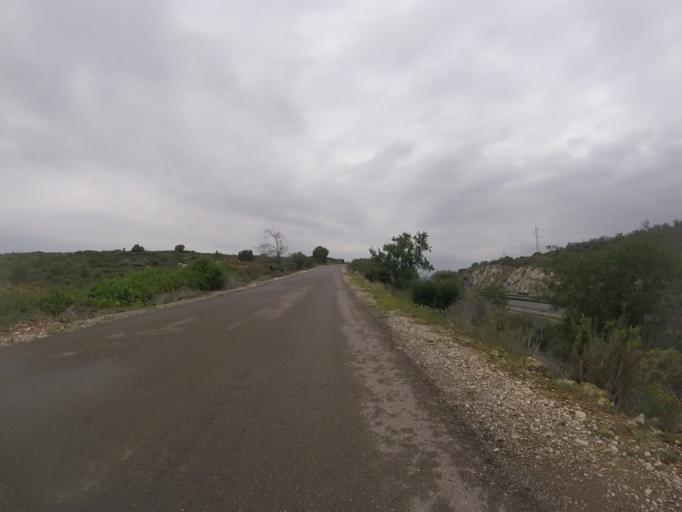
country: ES
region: Valencia
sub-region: Provincia de Castello
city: Alcala de Xivert
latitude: 40.2803
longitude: 0.2295
